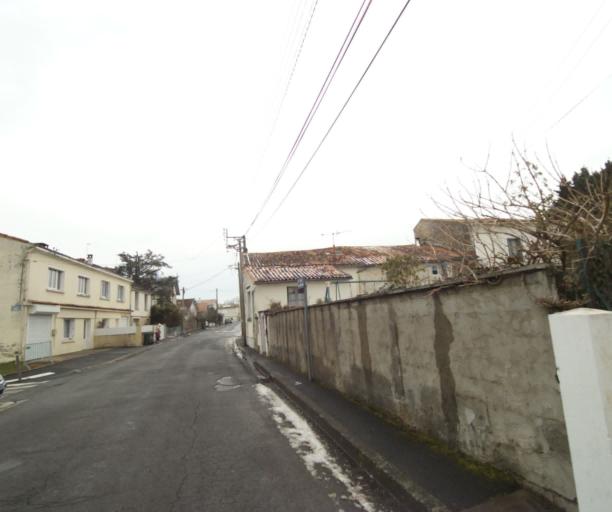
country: FR
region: Poitou-Charentes
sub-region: Departement des Deux-Sevres
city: Niort
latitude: 46.3226
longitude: -0.4794
